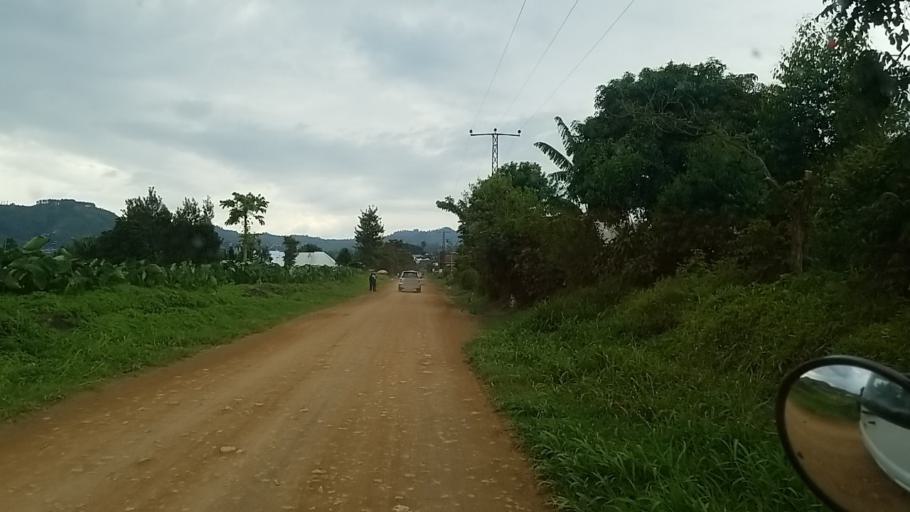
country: CD
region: Nord Kivu
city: Sake
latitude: -1.6837
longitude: 29.0162
